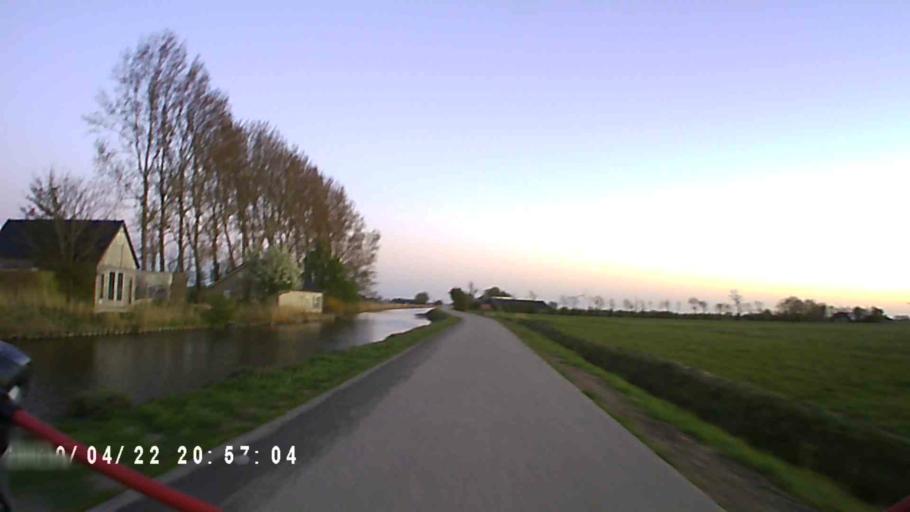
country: NL
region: Groningen
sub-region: Gemeente Winsum
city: Winsum
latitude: 53.3296
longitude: 6.5659
